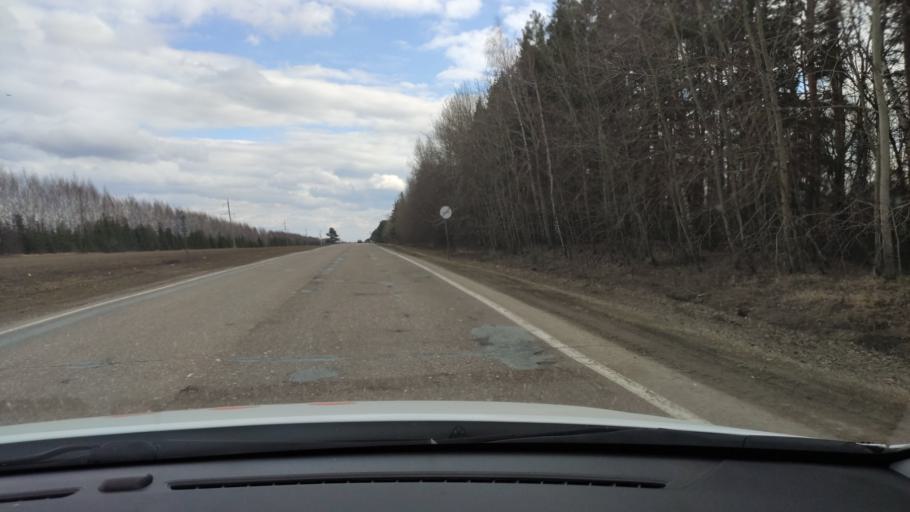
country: RU
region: Tatarstan
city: Vysokaya Gora
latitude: 56.0612
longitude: 49.2047
